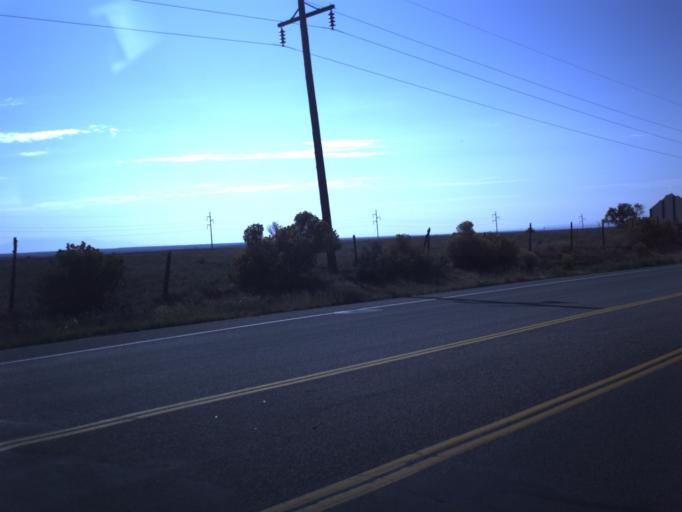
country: US
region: Utah
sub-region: San Juan County
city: Blanding
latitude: 37.5949
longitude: -109.4786
